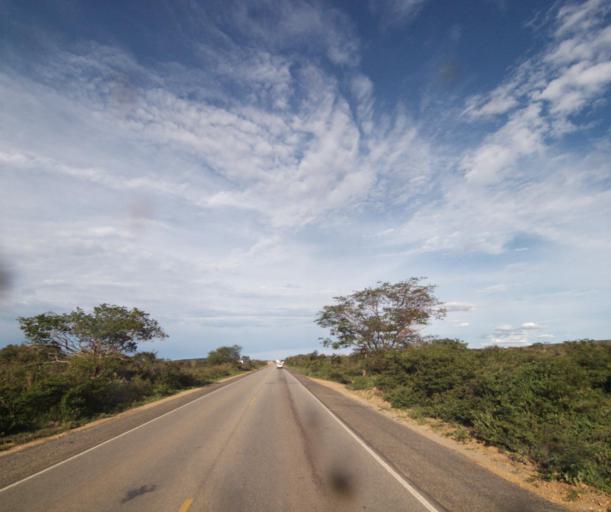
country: BR
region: Bahia
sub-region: Caetite
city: Caetite
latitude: -14.0759
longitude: -42.5473
